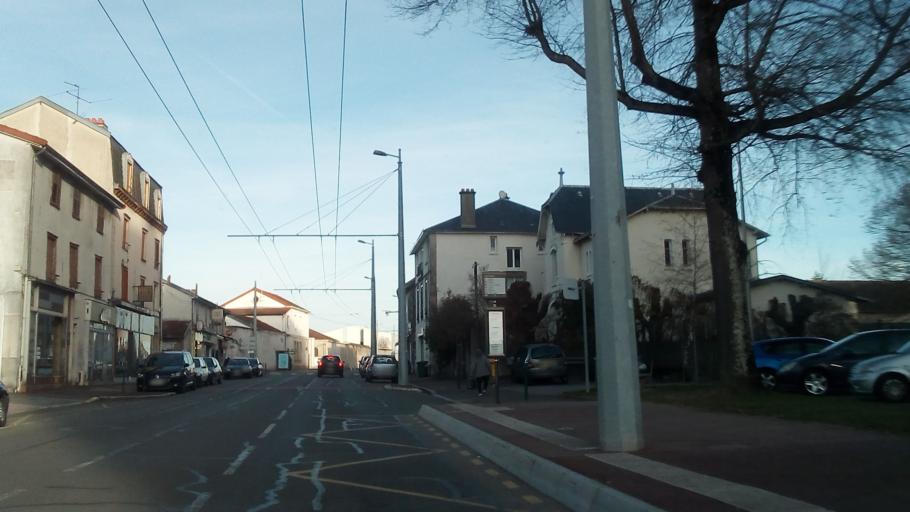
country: FR
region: Limousin
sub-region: Departement de la Haute-Vienne
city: Limoges
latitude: 45.8419
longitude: 1.2460
